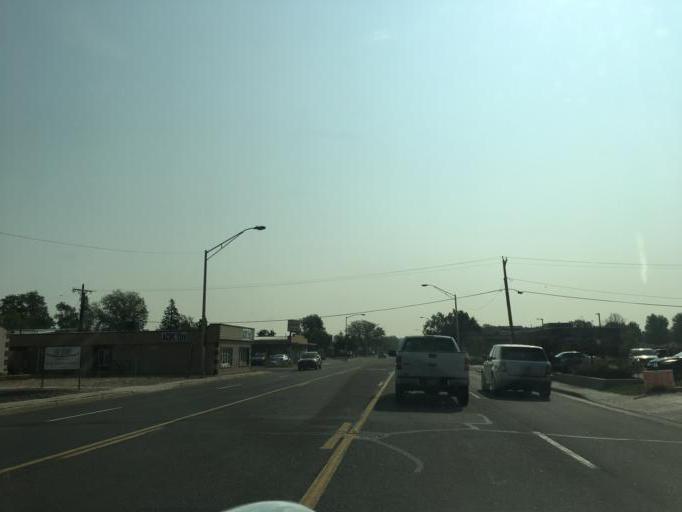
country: US
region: Colorado
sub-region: Adams County
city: Brighton
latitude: 39.9868
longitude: -104.8080
